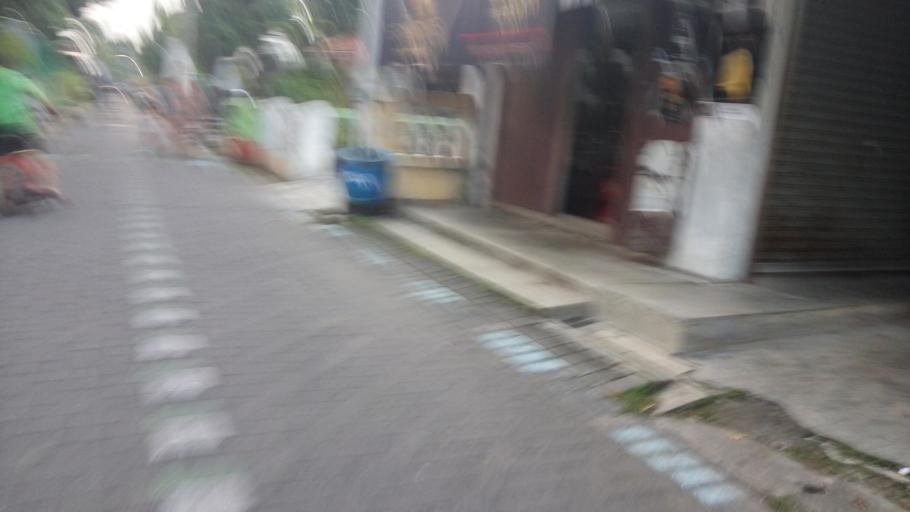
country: ID
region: Central Java
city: Semarang
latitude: -6.9864
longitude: 110.4043
